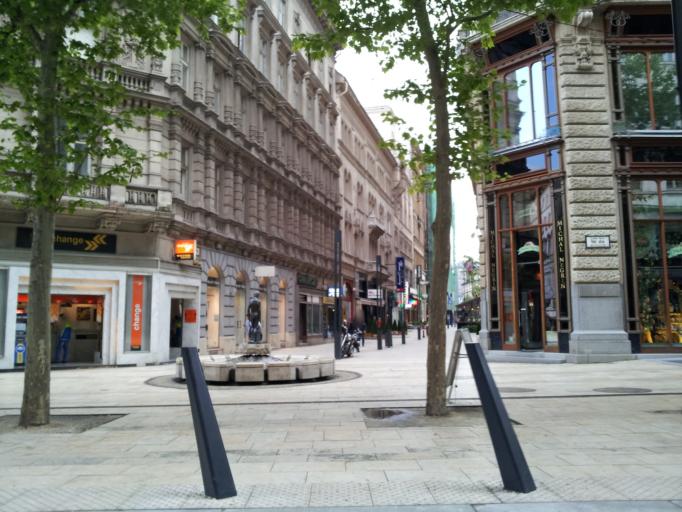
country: HU
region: Budapest
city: Budapest I. keruelet
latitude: 47.4930
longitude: 19.0530
